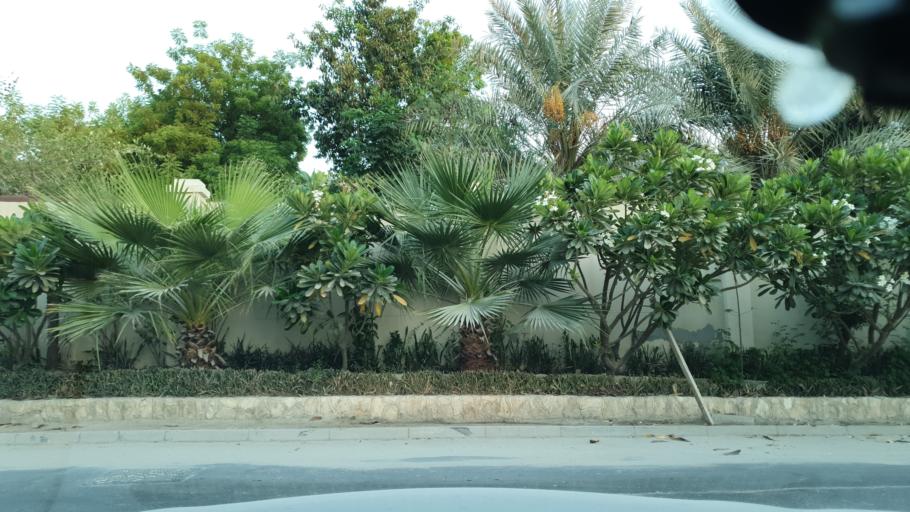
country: BH
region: Northern
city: Madinat `Isa
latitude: 26.1576
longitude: 50.5634
